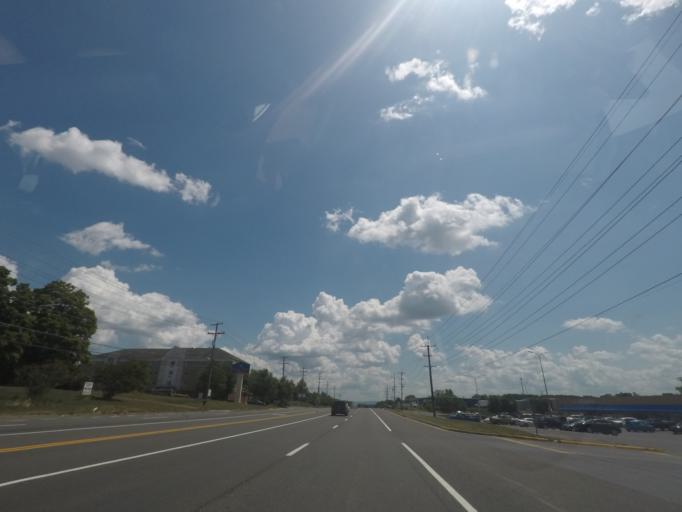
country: US
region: Virginia
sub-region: City of Winchester
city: Winchester
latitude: 39.1592
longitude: -78.1512
